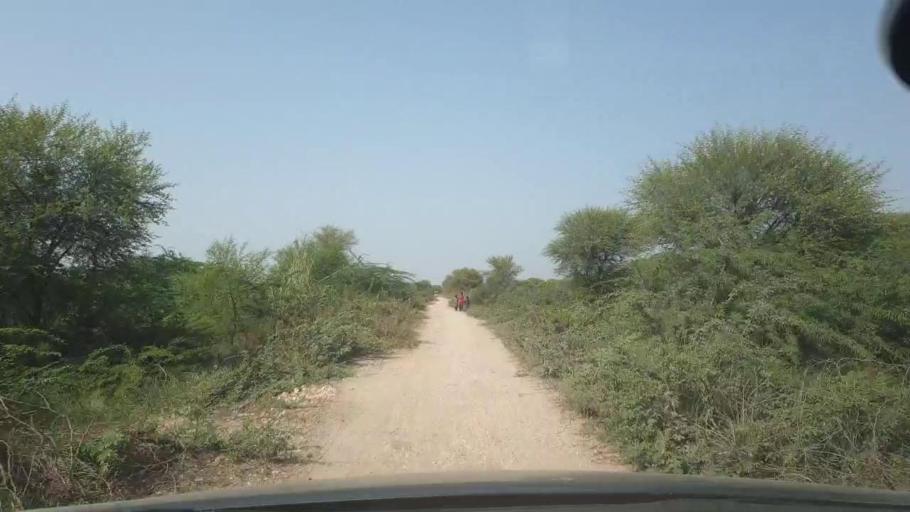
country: PK
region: Sindh
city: Naukot
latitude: 24.7982
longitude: 69.2410
